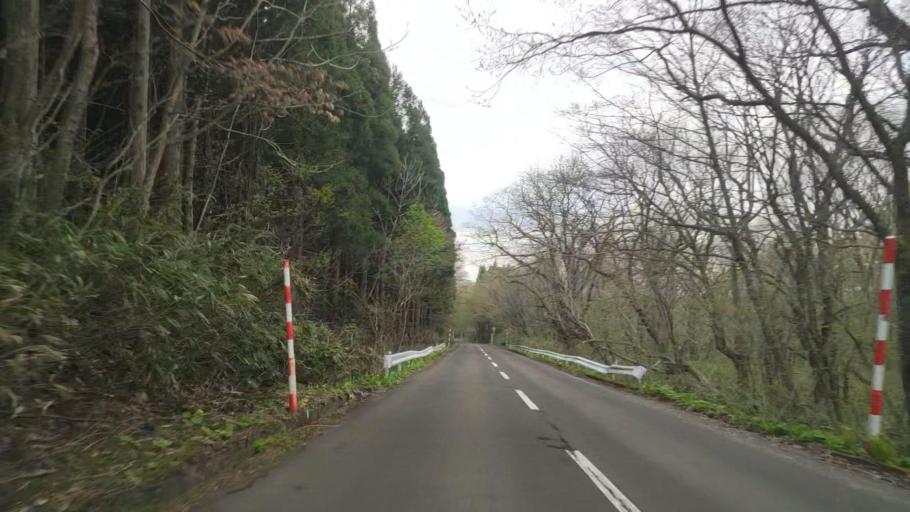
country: JP
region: Akita
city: Hanawa
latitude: 40.3953
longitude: 140.7966
